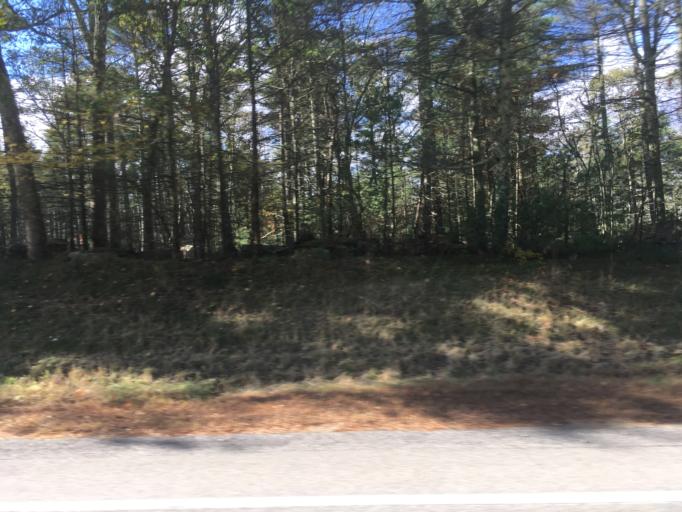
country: US
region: Rhode Island
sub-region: Providence County
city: North Scituate
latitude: 41.7857
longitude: -71.5934
